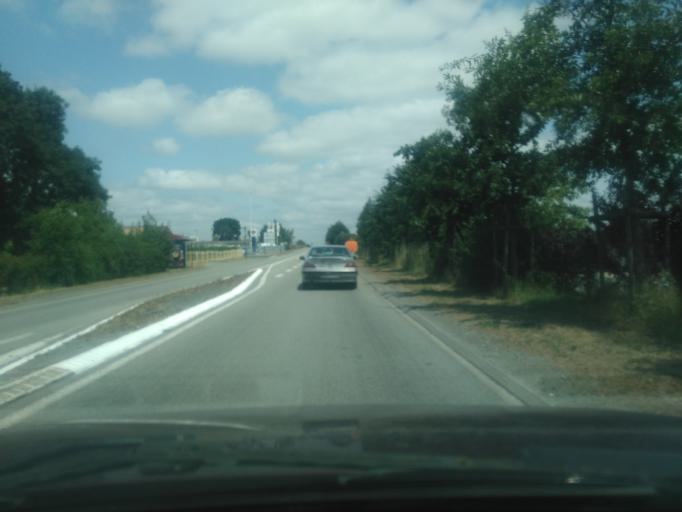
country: FR
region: Pays de la Loire
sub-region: Departement de la Vendee
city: Vendrennes
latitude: 46.7979
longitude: -1.1528
